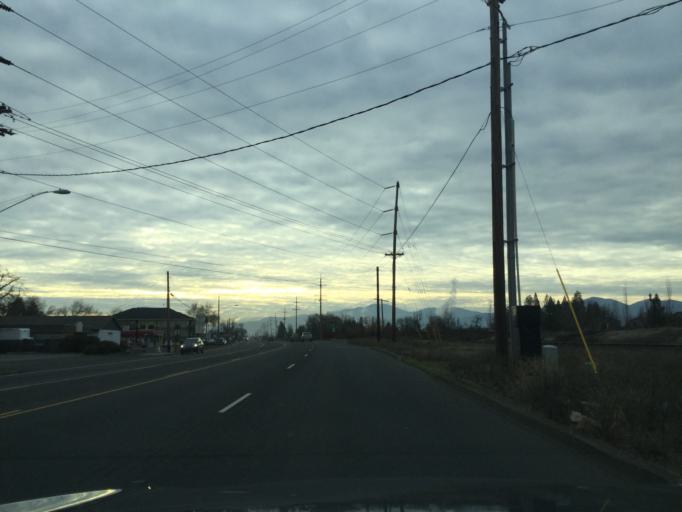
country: US
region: Oregon
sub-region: Jackson County
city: Central Point
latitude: 42.3692
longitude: -122.9140
